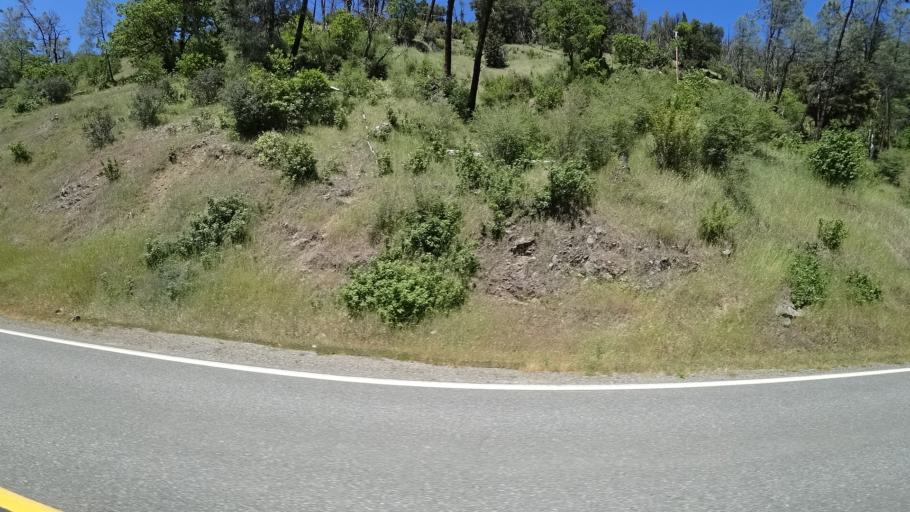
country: US
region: California
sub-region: Trinity County
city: Hayfork
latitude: 40.7393
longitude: -123.2431
